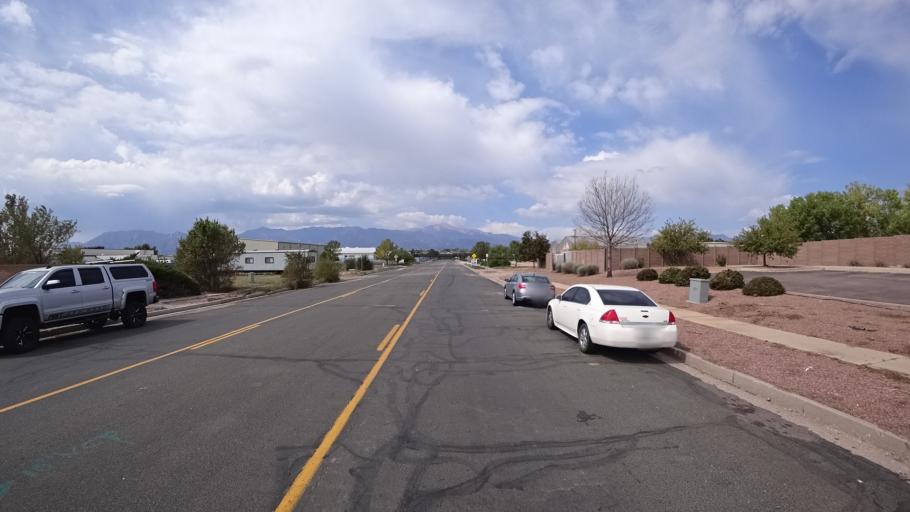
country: US
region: Colorado
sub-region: El Paso County
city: Cimarron Hills
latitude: 38.8442
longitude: -104.7344
